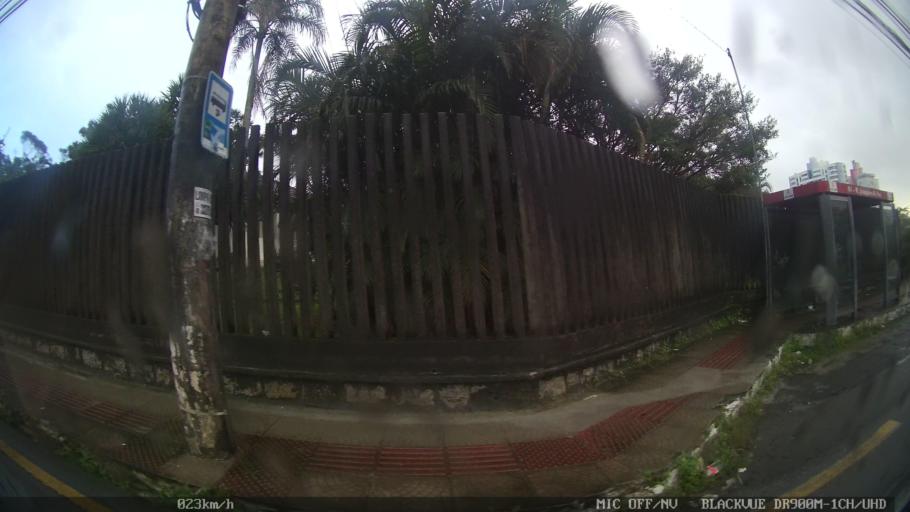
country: BR
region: Santa Catarina
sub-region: Sao Jose
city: Campinas
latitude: -27.6034
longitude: -48.6210
